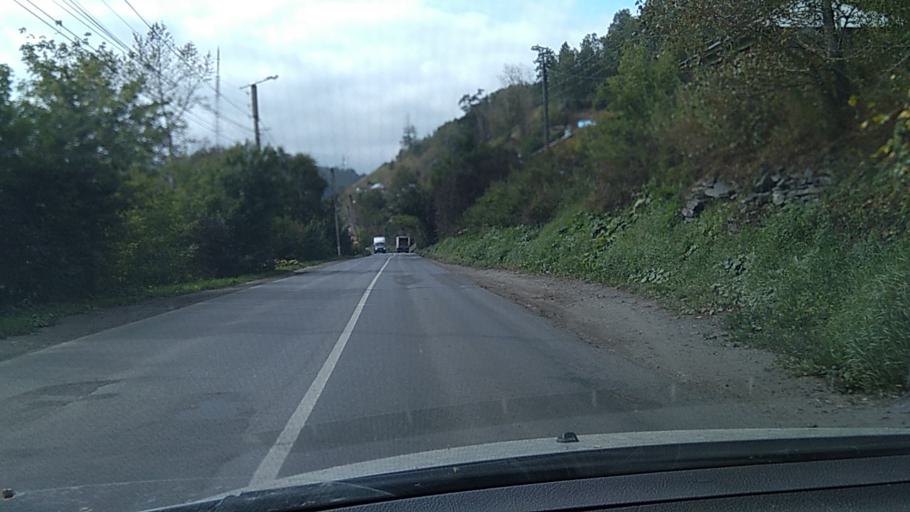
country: RU
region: Chelyabinsk
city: Zlatoust
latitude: 55.1754
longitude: 59.6875
